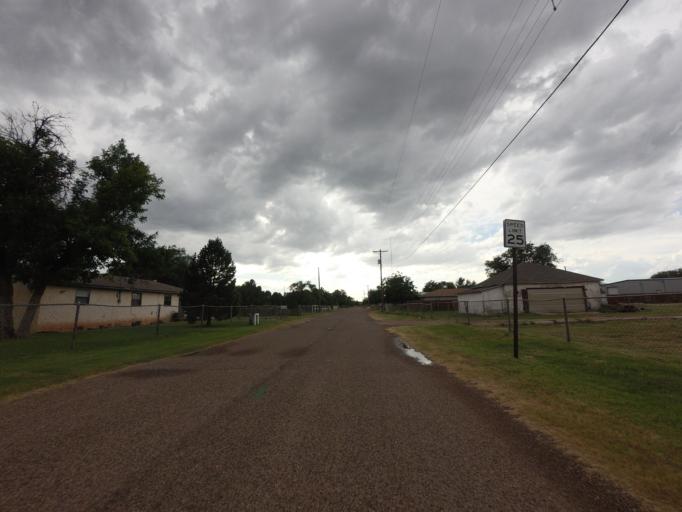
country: US
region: New Mexico
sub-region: Curry County
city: Clovis
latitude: 34.3880
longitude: -103.1818
